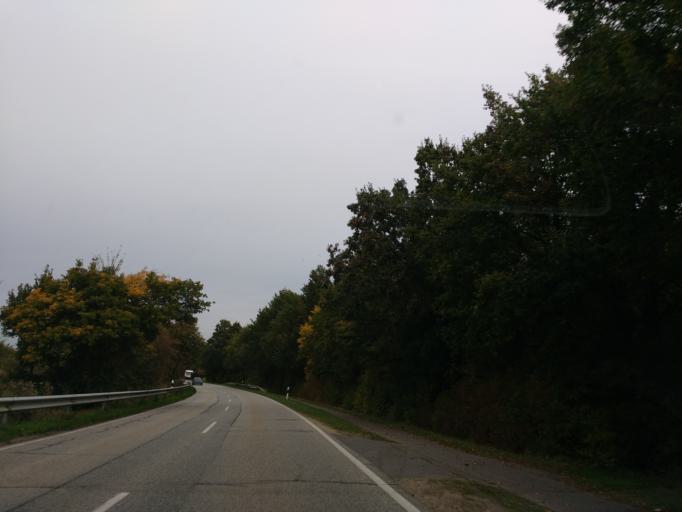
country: DE
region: Schleswig-Holstein
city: Gromitz
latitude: 54.1588
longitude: 10.9634
